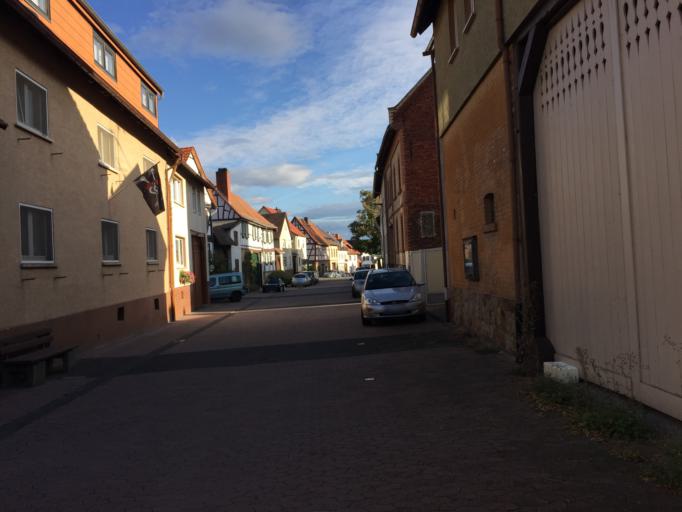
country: DE
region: Hesse
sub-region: Regierungsbezirk Darmstadt
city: Munzenberg
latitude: 50.4644
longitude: 8.7489
